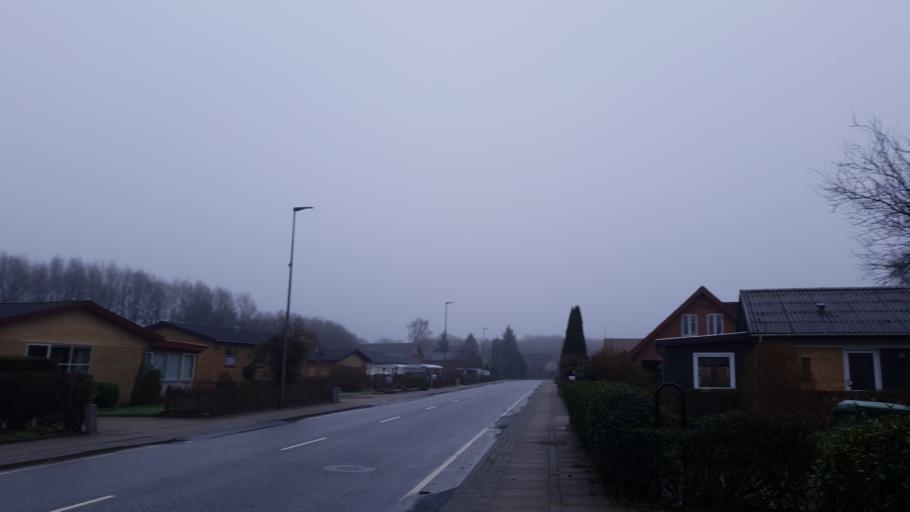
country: DK
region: Central Jutland
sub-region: Hedensted Kommune
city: Hedensted
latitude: 55.7979
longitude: 9.6984
